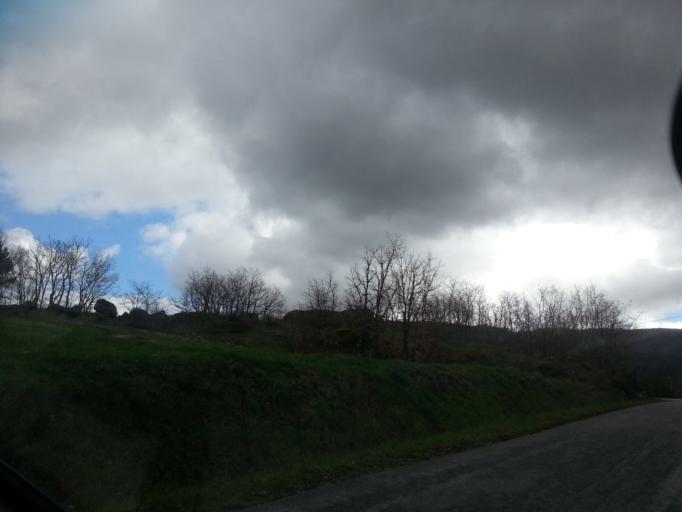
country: PT
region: Guarda
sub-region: Fornos de Algodres
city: Fornos de Algodres
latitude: 40.5640
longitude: -7.4625
